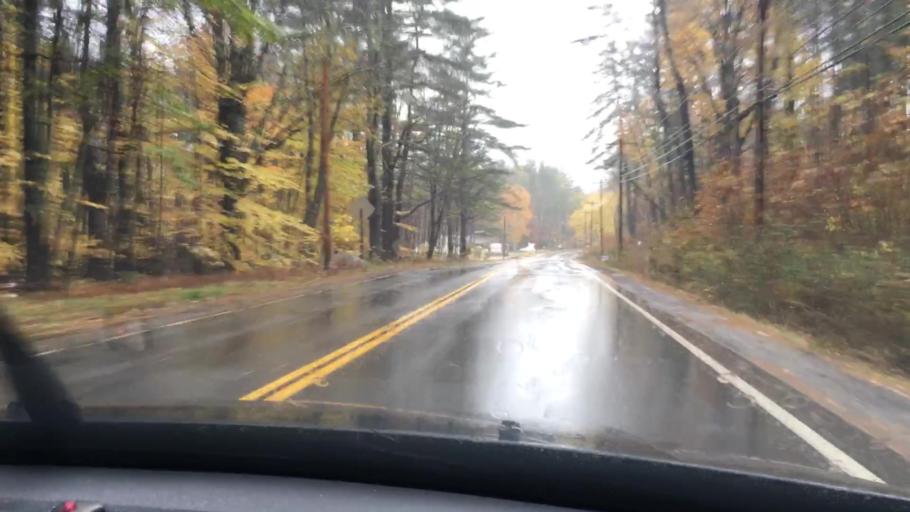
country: US
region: New Hampshire
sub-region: Grafton County
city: Holderness
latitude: 43.7218
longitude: -71.5521
